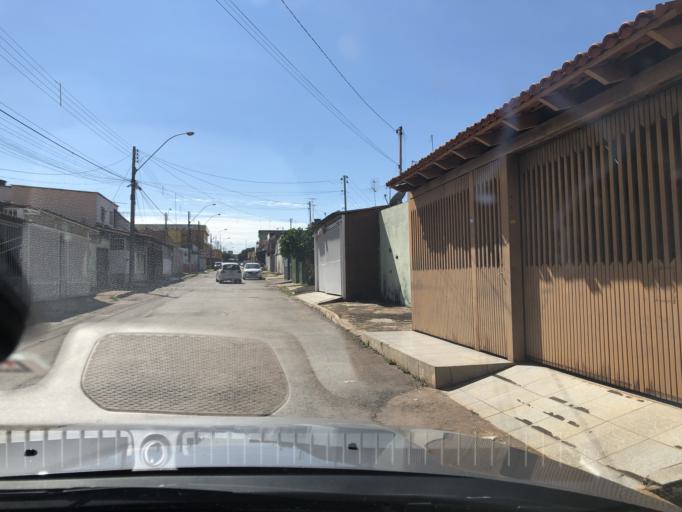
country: BR
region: Federal District
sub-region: Brasilia
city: Brasilia
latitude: -15.8052
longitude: -48.1414
